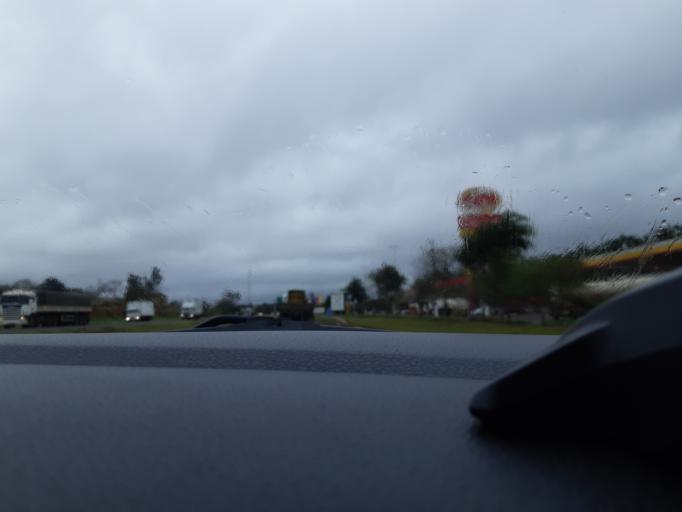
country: BR
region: Sao Paulo
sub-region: Ourinhos
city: Ourinhos
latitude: -22.9820
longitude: -49.9035
